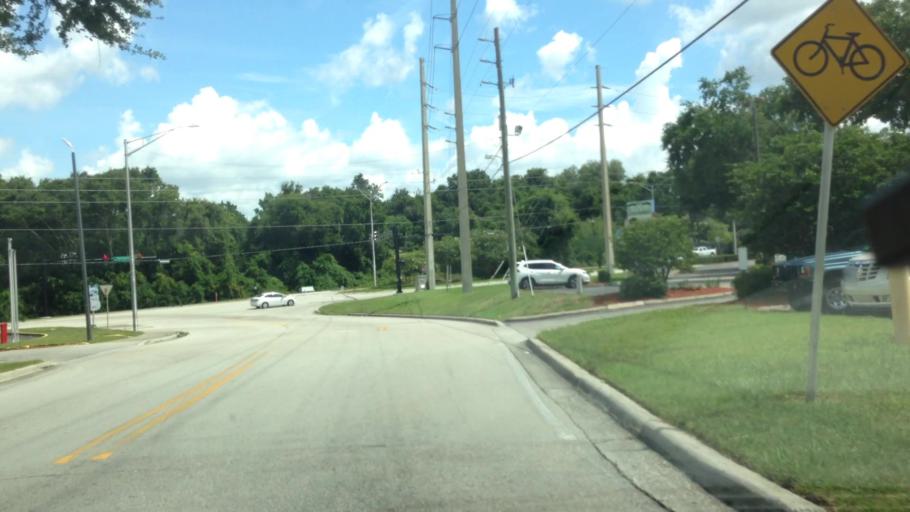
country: US
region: Florida
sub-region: Duval County
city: Jacksonville
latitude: 30.3418
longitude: -81.5373
